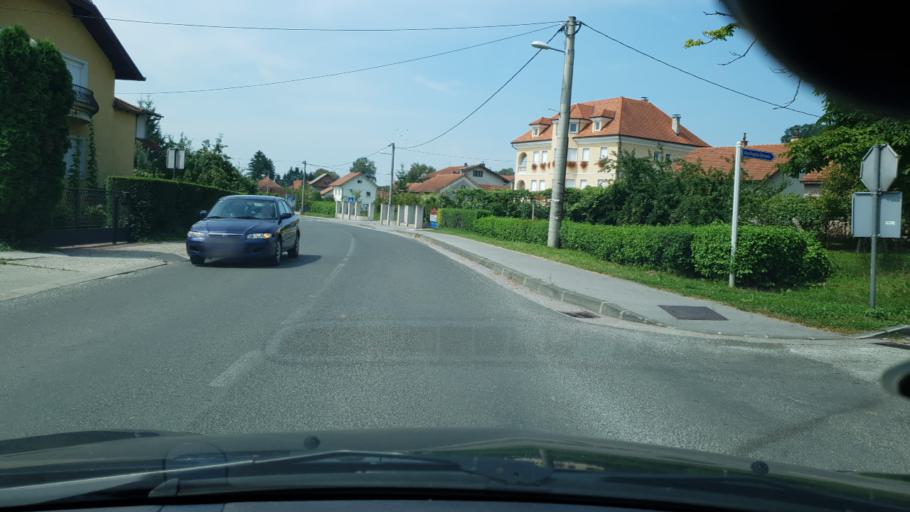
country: HR
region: Krapinsko-Zagorska
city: Bedekovcina
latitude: 46.0420
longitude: 15.9945
